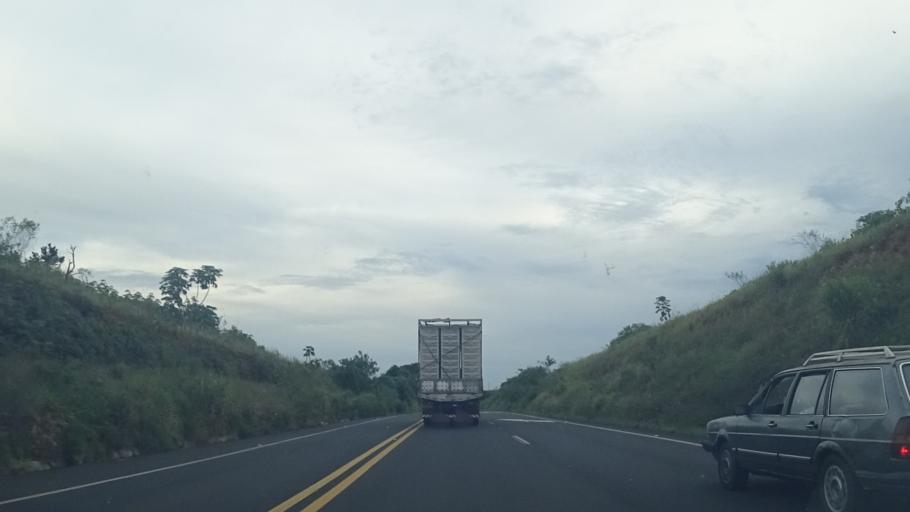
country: BR
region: Sao Paulo
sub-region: Martinopolis
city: Martinopolis
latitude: -22.1114
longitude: -51.1600
